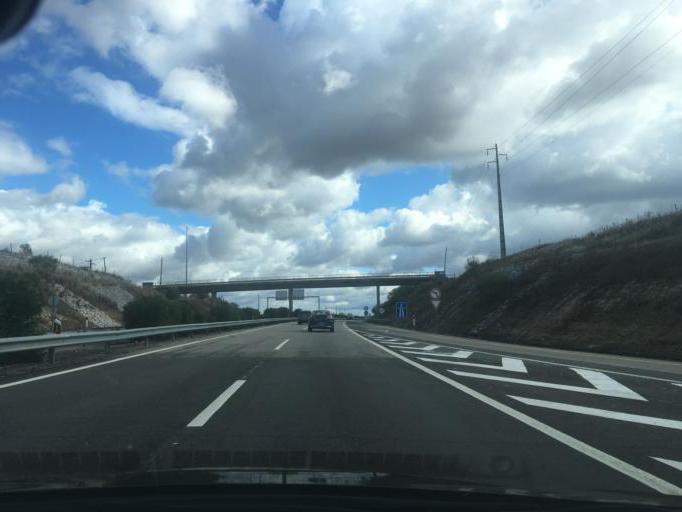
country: PT
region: Santarem
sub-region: Alcanena
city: Alcanena
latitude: 39.4798
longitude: -8.6198
